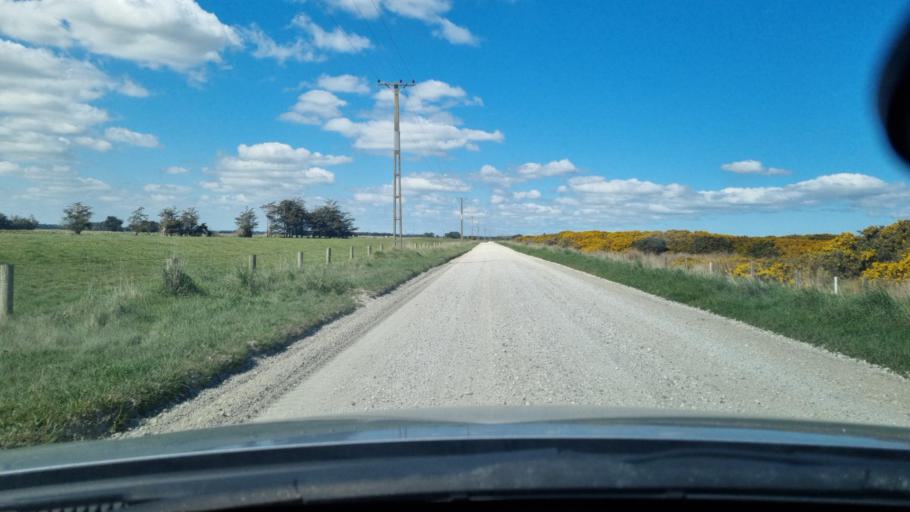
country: NZ
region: Southland
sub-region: Invercargill City
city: Invercargill
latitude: -46.3915
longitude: 168.2659
